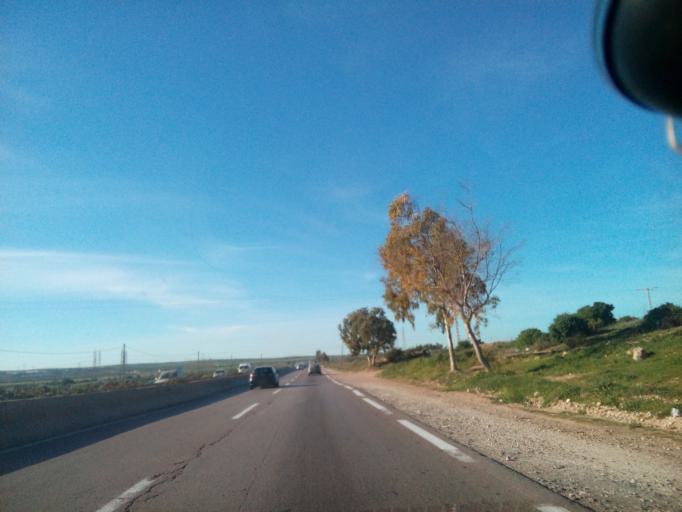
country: DZ
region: Oran
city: Ain el Bya
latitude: 35.7756
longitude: -0.1936
